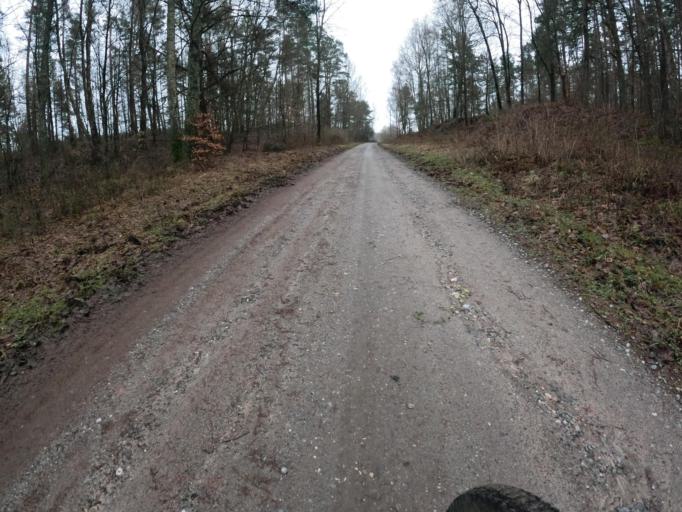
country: PL
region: West Pomeranian Voivodeship
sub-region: Powiat slawienski
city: Slawno
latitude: 54.2418
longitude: 16.6450
